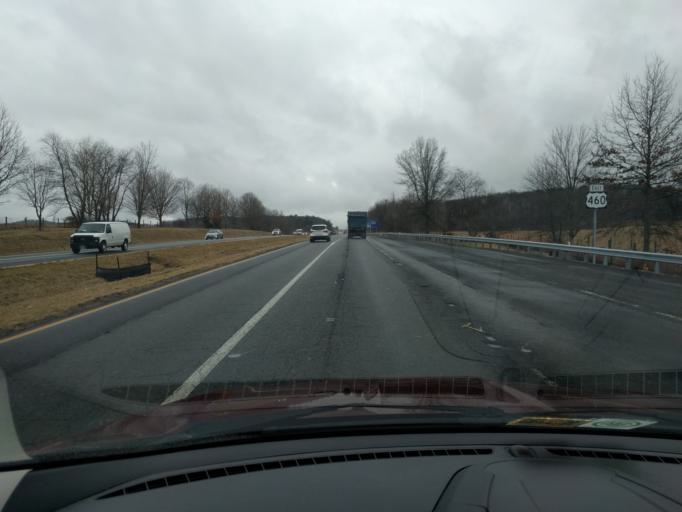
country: US
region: Virginia
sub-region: Montgomery County
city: Merrimac
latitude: 37.2062
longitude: -80.4226
